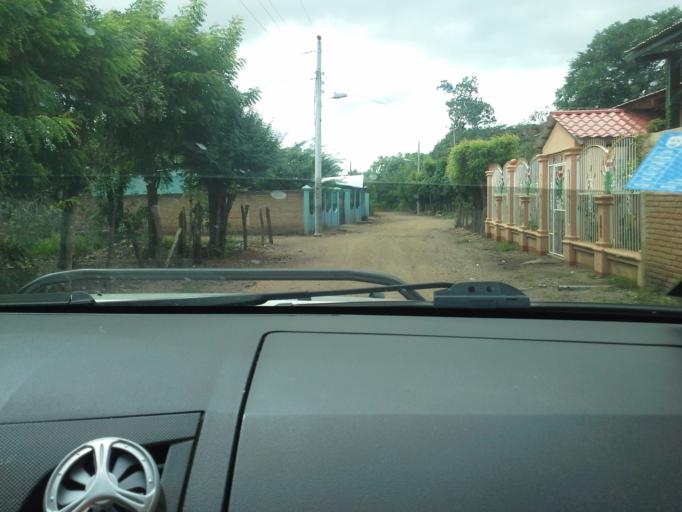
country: NI
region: Matagalpa
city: Ciudad Dario
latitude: 12.8360
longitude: -86.2156
